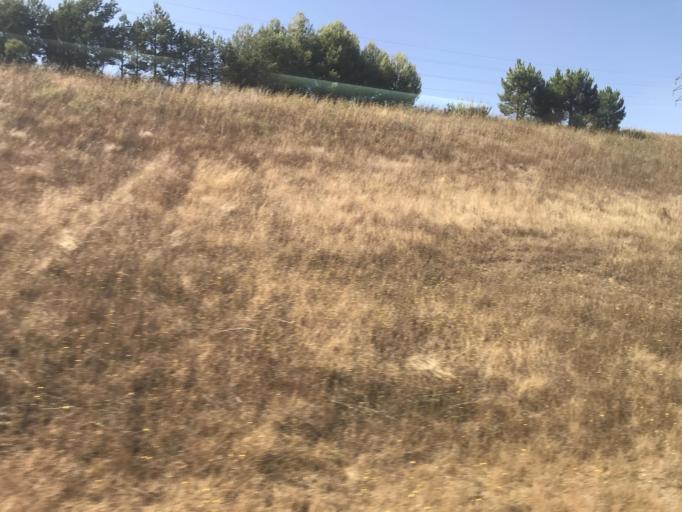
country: ES
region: Castille and Leon
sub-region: Provincia de Burgos
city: Hurones
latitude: 42.3740
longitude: -3.6392
